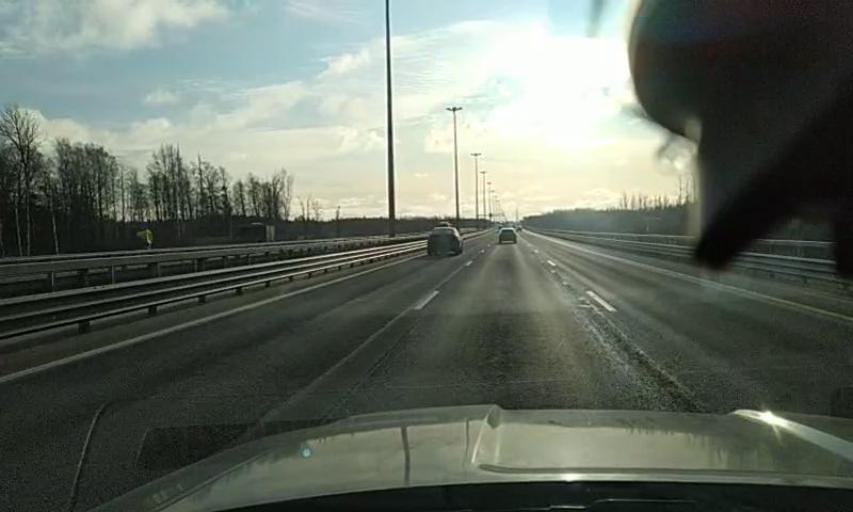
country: RU
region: St.-Petersburg
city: Pesochnyy
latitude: 60.1091
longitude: 30.0835
